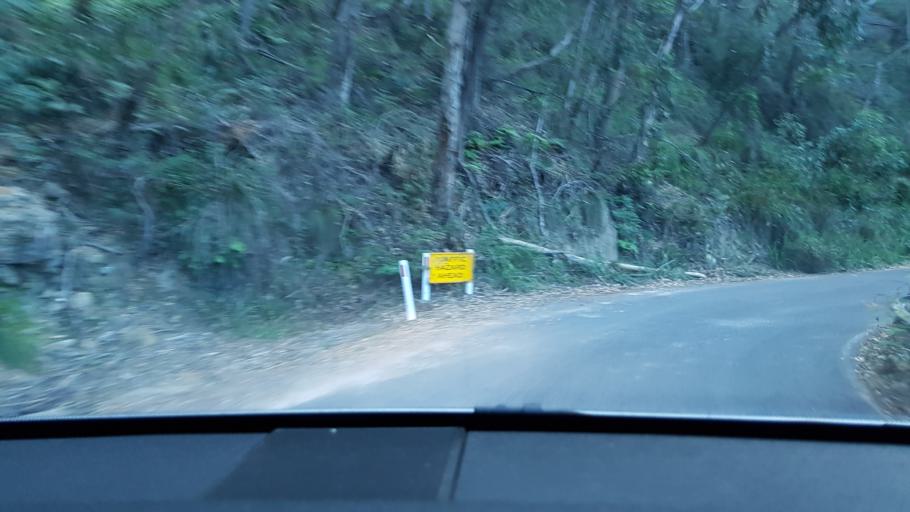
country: AU
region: New South Wales
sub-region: Lithgow
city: Portland
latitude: -33.3113
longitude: 150.1100
